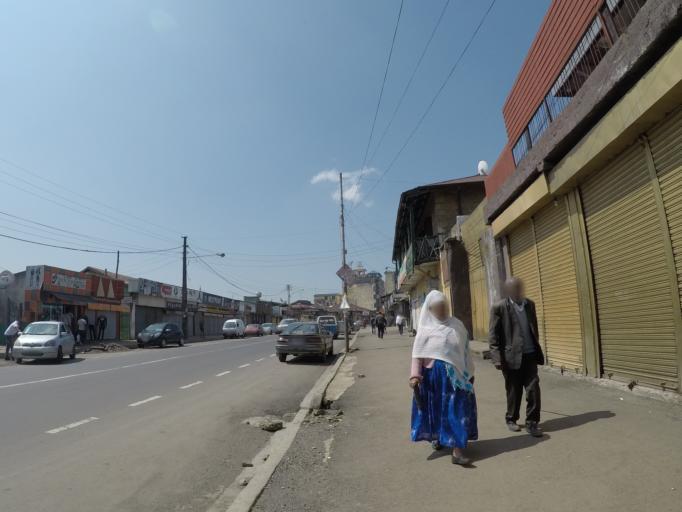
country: ET
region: Adis Abeba
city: Addis Ababa
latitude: 9.0368
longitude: 38.7528
